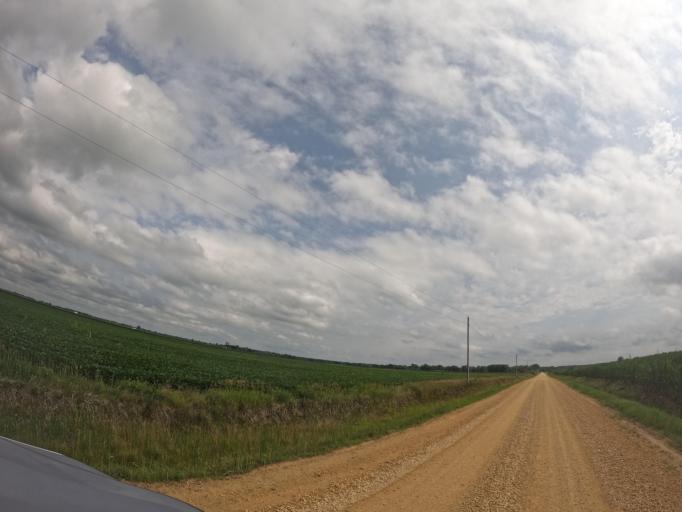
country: US
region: Iowa
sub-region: Clinton County
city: De Witt
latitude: 41.7836
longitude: -90.5828
